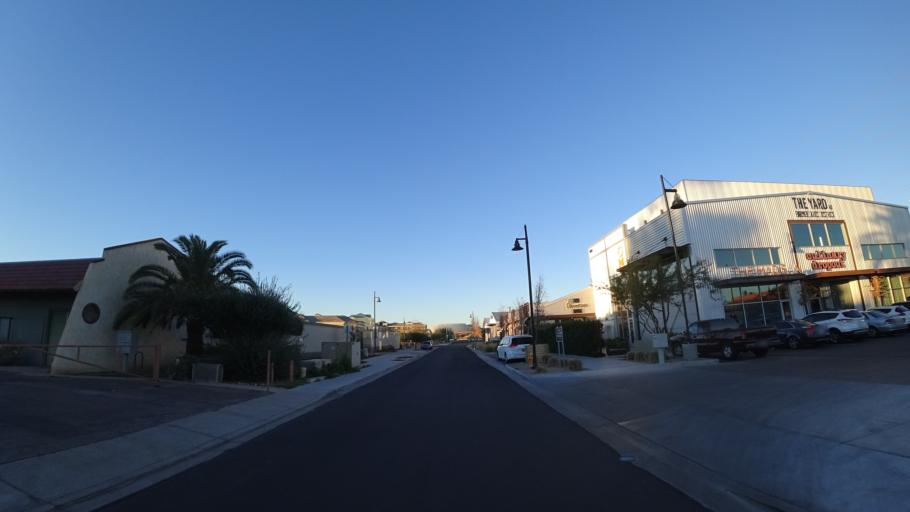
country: US
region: Arizona
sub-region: Maricopa County
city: Tempe Junction
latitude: 33.4282
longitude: -111.9443
